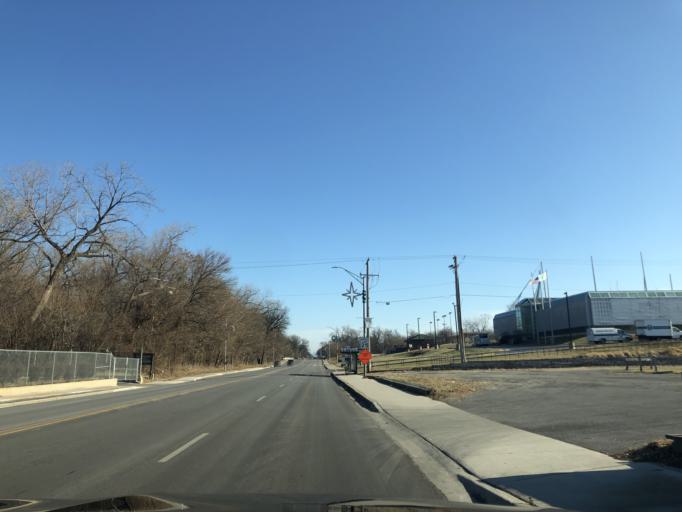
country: US
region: Illinois
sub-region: Cook County
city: Maywood
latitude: 41.8790
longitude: -87.8312
